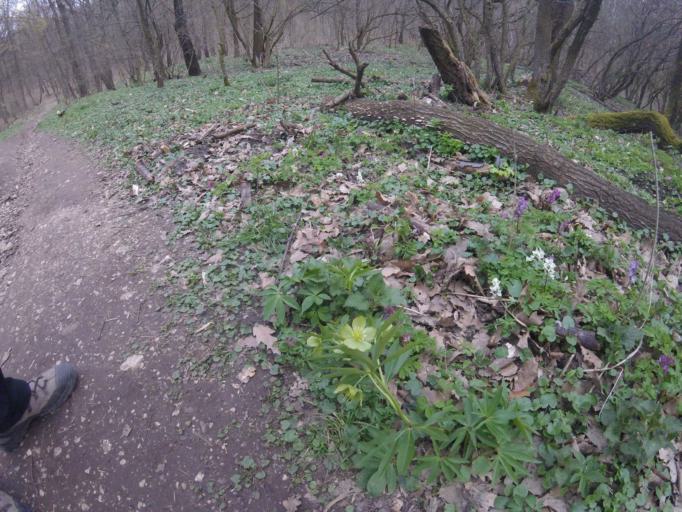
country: HU
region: Komarom-Esztergom
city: Oroszlany
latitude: 47.4806
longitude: 18.3973
